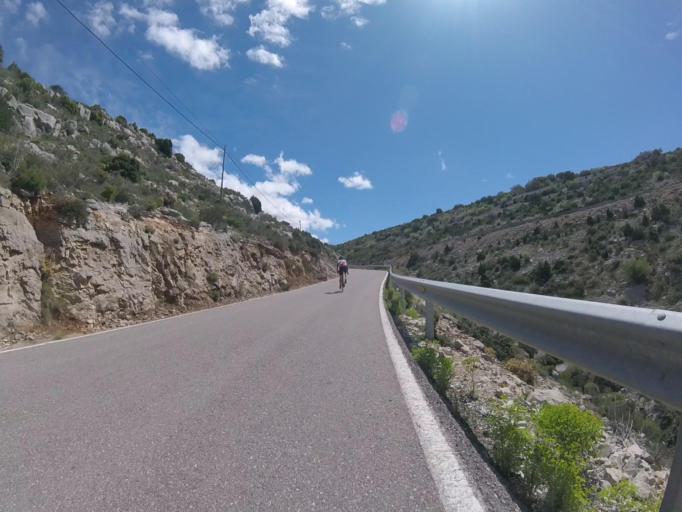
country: ES
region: Valencia
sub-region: Provincia de Castello
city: Sierra-Engarceran
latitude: 40.2788
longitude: -0.0304
